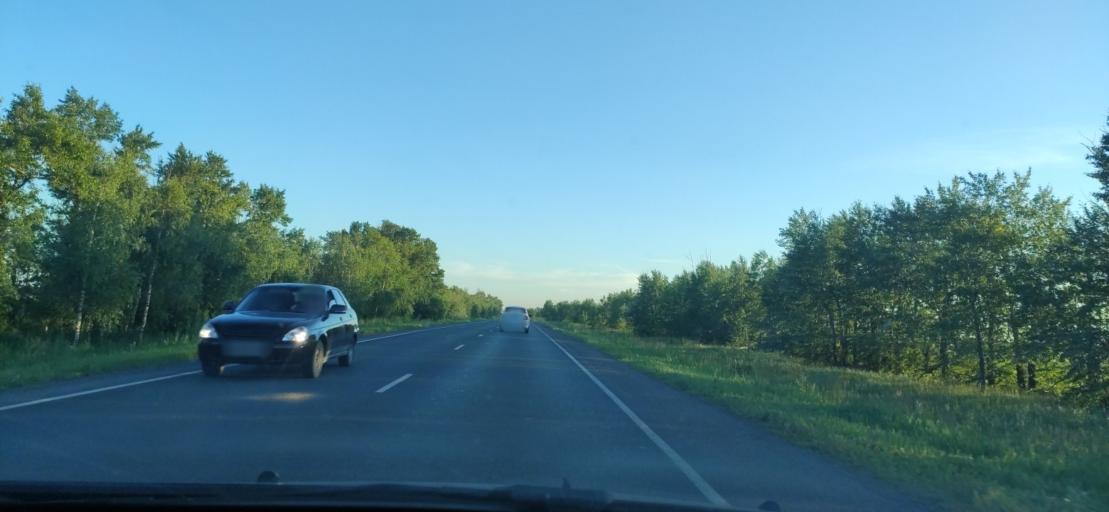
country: RU
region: Ulyanovsk
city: Cherdakly
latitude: 54.4035
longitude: 48.8663
